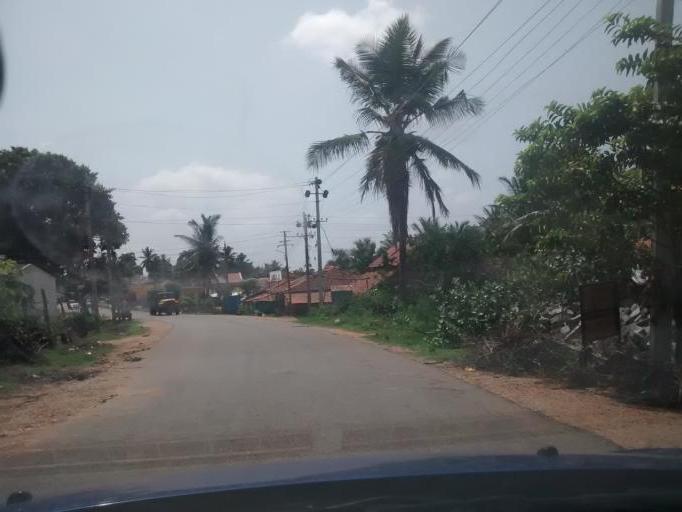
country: IN
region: Karnataka
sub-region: Hassan
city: Konanur
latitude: 12.5808
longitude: 76.2052
